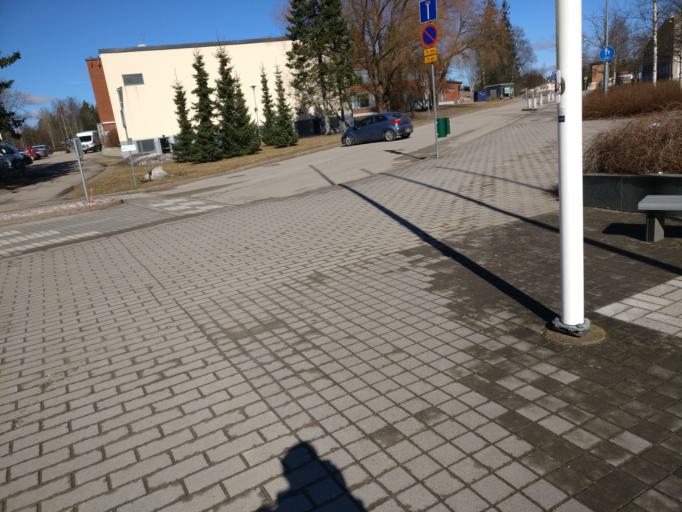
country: FI
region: Uusimaa
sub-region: Helsinki
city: Jaervenpaeae
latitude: 60.4810
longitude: 25.0808
